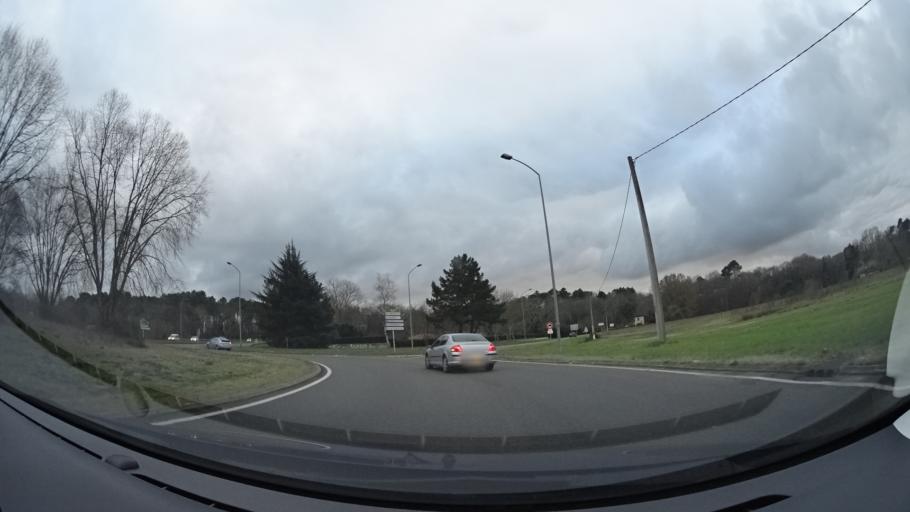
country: FR
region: Aquitaine
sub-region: Departement des Landes
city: Mont-de-Marsan
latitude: 43.8900
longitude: -0.4449
